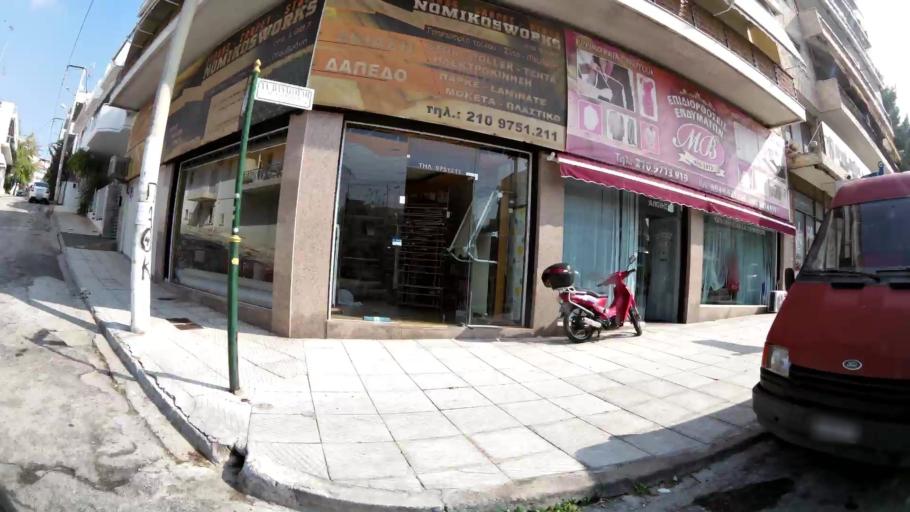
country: GR
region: Attica
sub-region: Nomarchia Athinas
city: Ilioupoli
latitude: 37.9420
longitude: 23.7604
